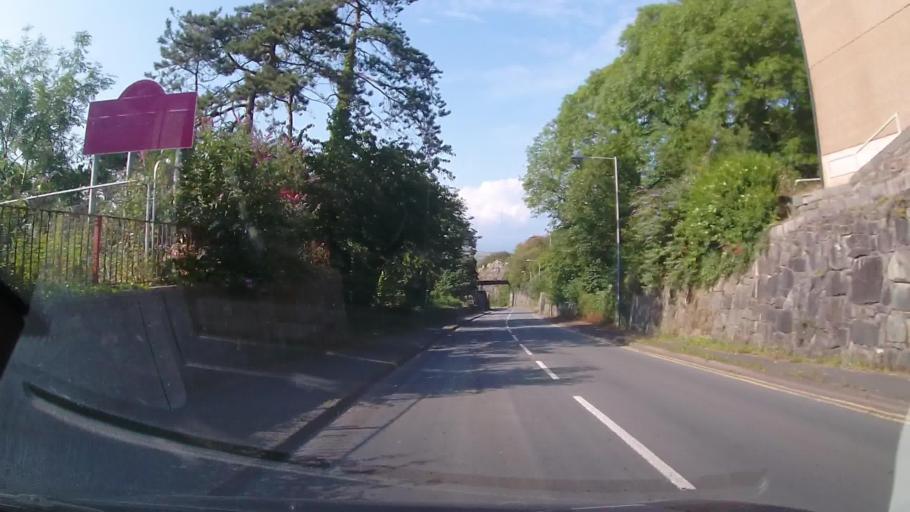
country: GB
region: Wales
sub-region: Gwynedd
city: Llanfair
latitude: 52.8544
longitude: -4.1129
